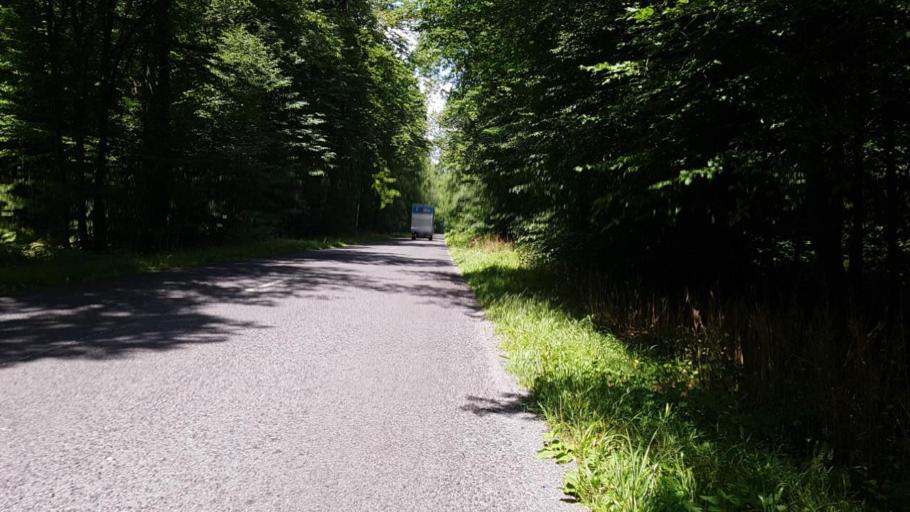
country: FR
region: Picardie
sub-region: Departement de l'Oise
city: Chiry-Ourscamp
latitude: 49.5370
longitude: 2.9852
